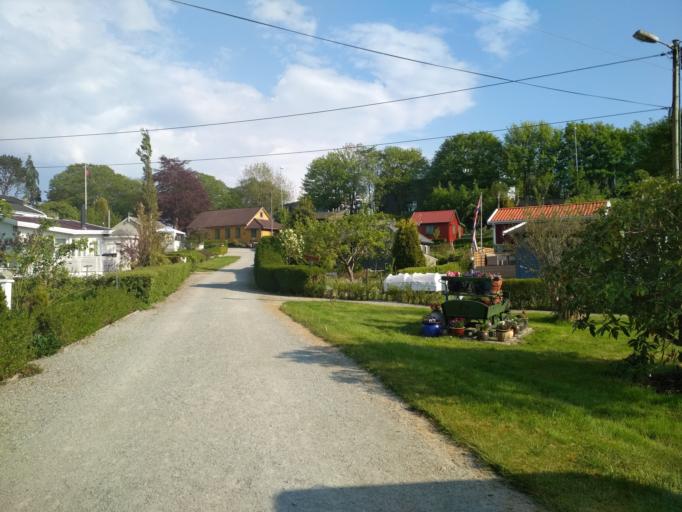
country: NO
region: Rogaland
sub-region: Stavanger
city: Stavanger
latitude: 58.9701
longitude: 5.7048
